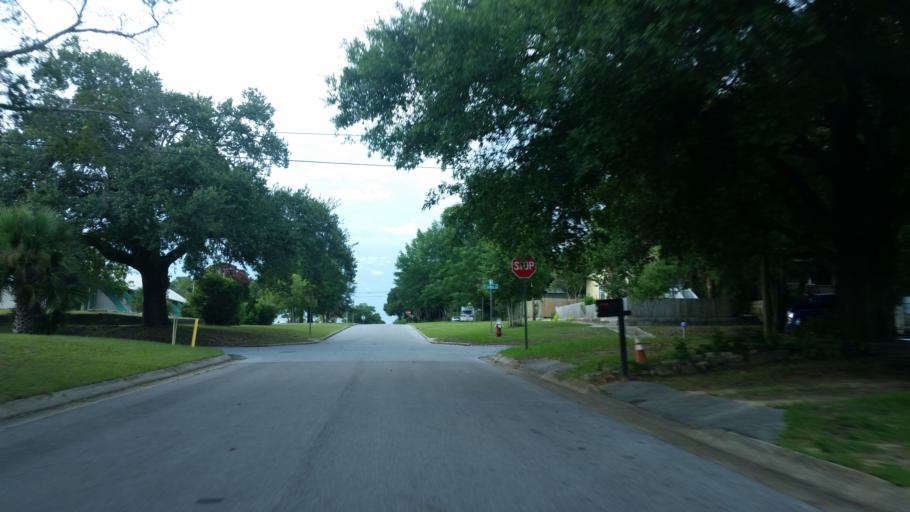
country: US
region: Florida
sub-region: Escambia County
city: Pensacola
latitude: 30.4202
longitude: -87.2049
